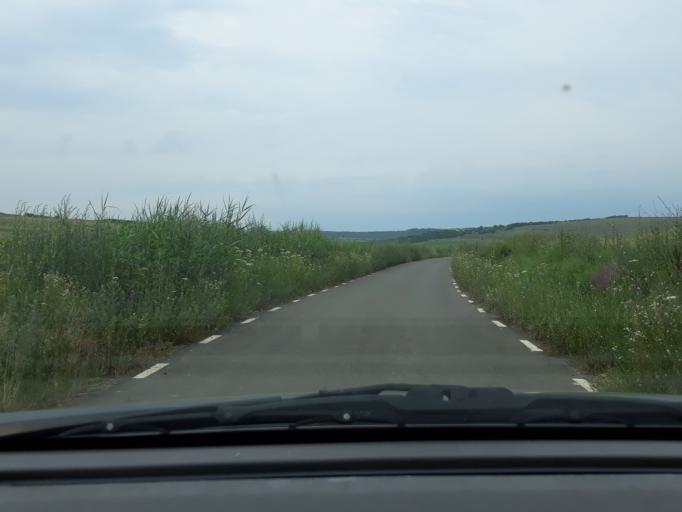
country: RO
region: Salaj
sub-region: Comuna Criseni
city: Criseni
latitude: 47.2762
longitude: 23.0799
